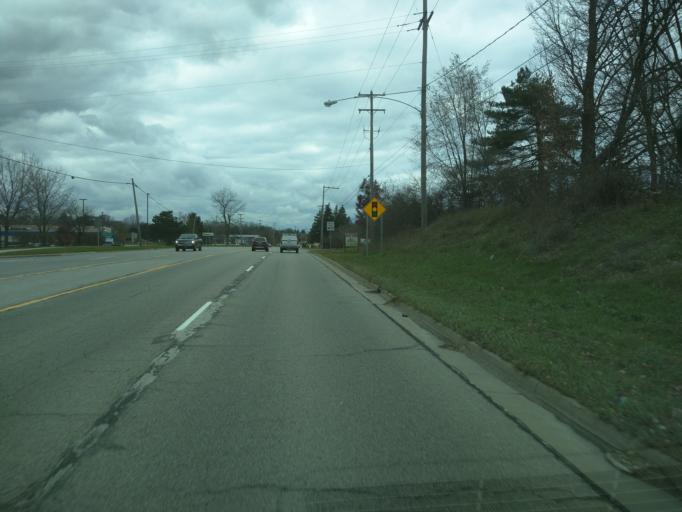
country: US
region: Michigan
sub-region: Ingham County
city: Okemos
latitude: 42.7168
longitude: -84.4051
